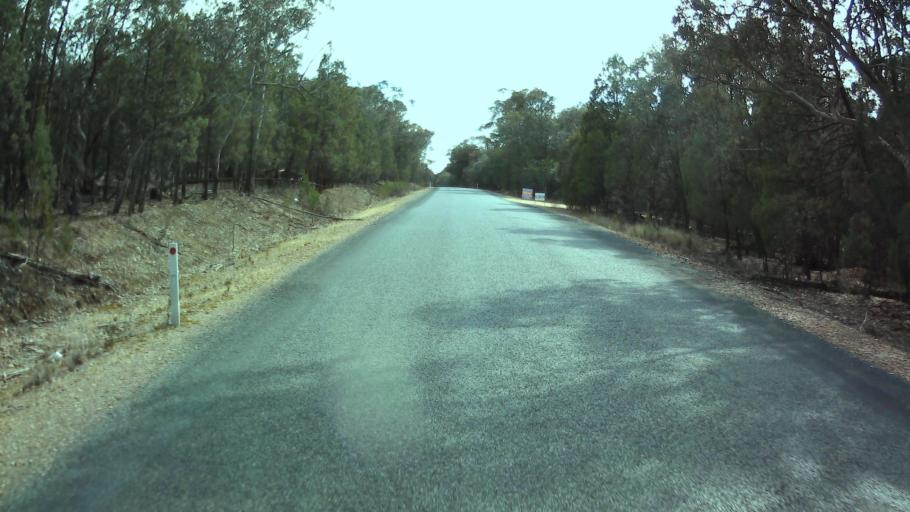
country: AU
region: New South Wales
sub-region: Weddin
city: Grenfell
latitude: -33.8947
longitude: 148.1873
